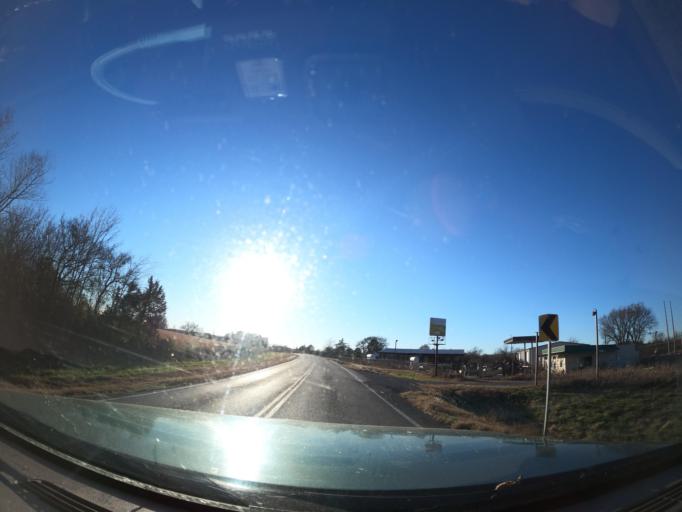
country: US
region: Oklahoma
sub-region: Latimer County
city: Wilburton
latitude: 34.9121
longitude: -95.4205
